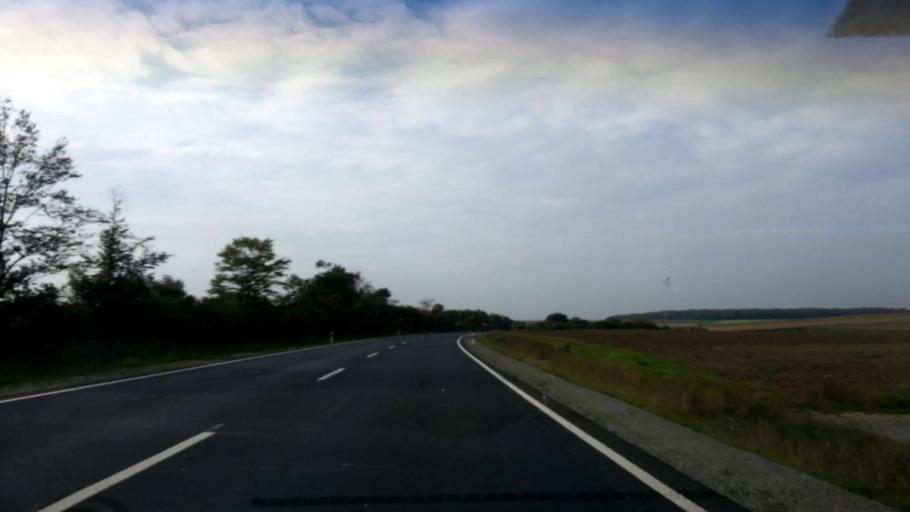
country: DE
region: Bavaria
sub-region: Regierungsbezirk Unterfranken
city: Lulsfeld
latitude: 49.8685
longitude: 10.3597
